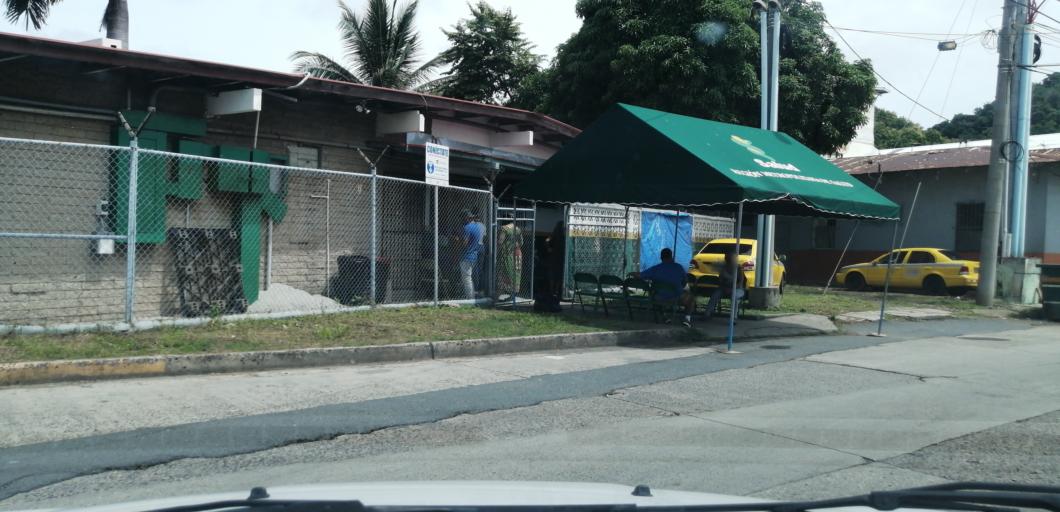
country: PA
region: Panama
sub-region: Distrito de Panama
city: Ancon
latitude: 8.9475
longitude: -79.5481
